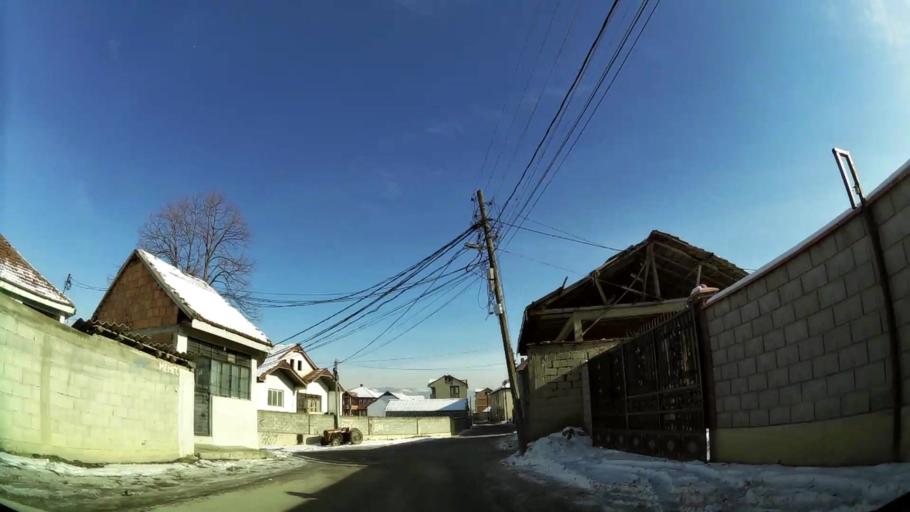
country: MK
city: Grchec
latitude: 41.9963
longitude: 21.3433
